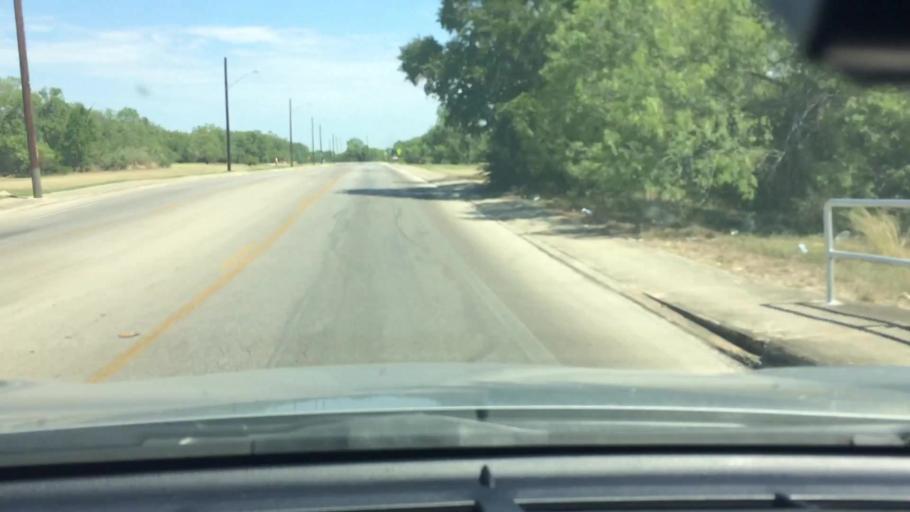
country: US
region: Texas
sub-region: Bexar County
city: San Antonio
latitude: 29.3833
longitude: -98.4306
